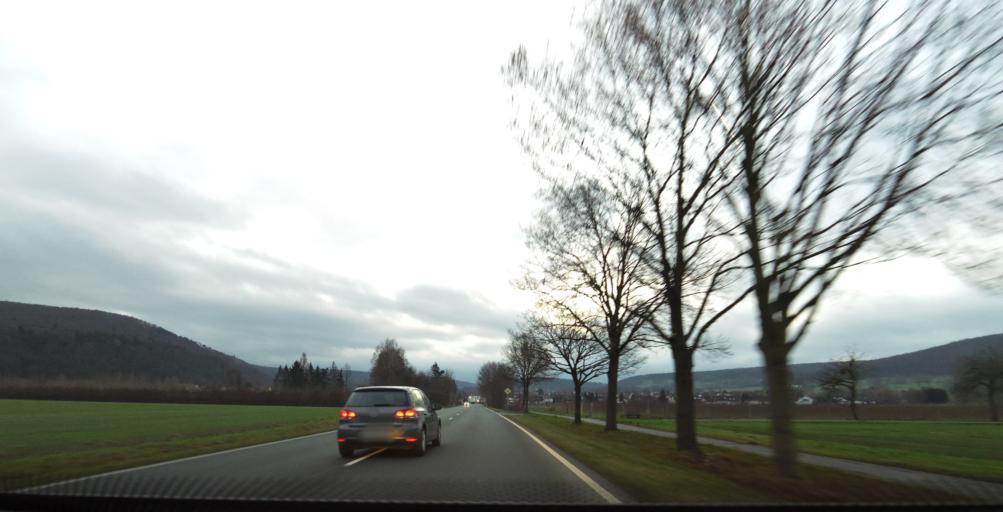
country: DE
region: Lower Saxony
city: Buhren
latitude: 51.4852
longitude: 9.6081
